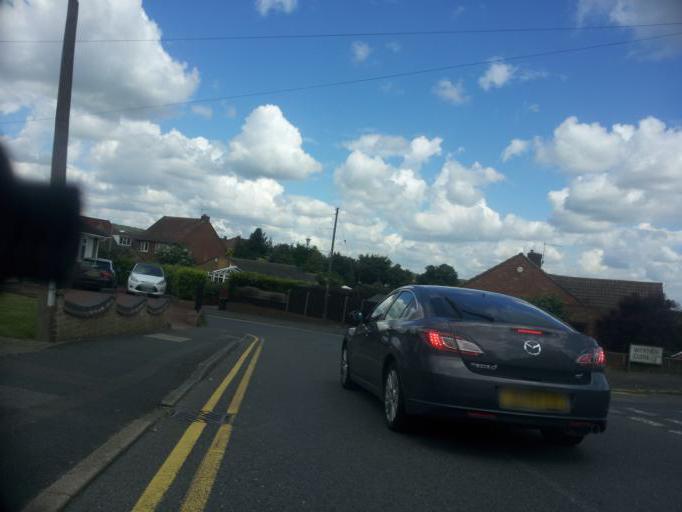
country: GB
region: England
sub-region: Kent
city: Snodland
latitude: 51.3250
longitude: 0.4389
